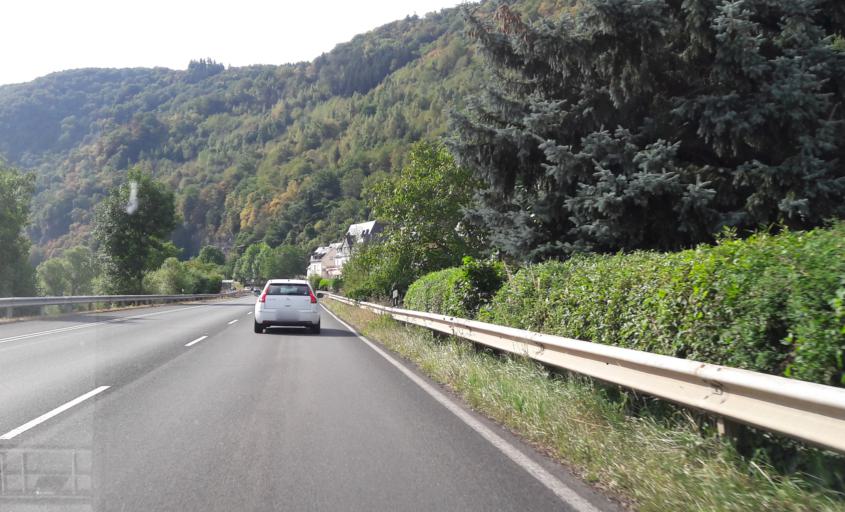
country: DE
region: Rheinland-Pfalz
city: Briedel
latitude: 50.0210
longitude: 7.1514
